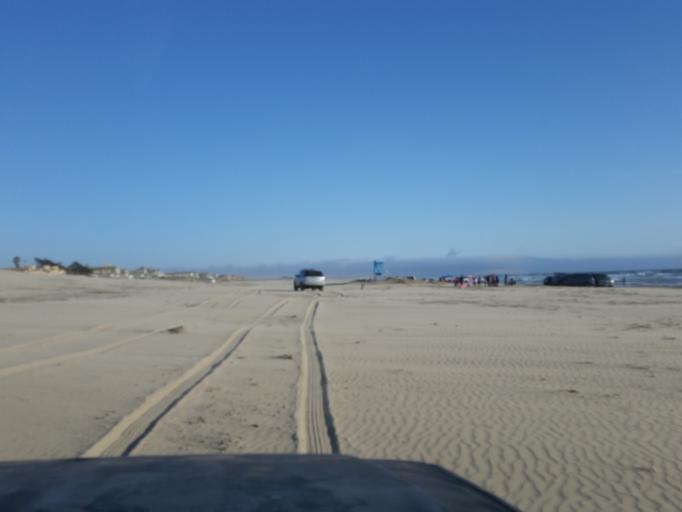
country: US
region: California
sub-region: San Luis Obispo County
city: Grover Beach
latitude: 35.1079
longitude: -120.6319
